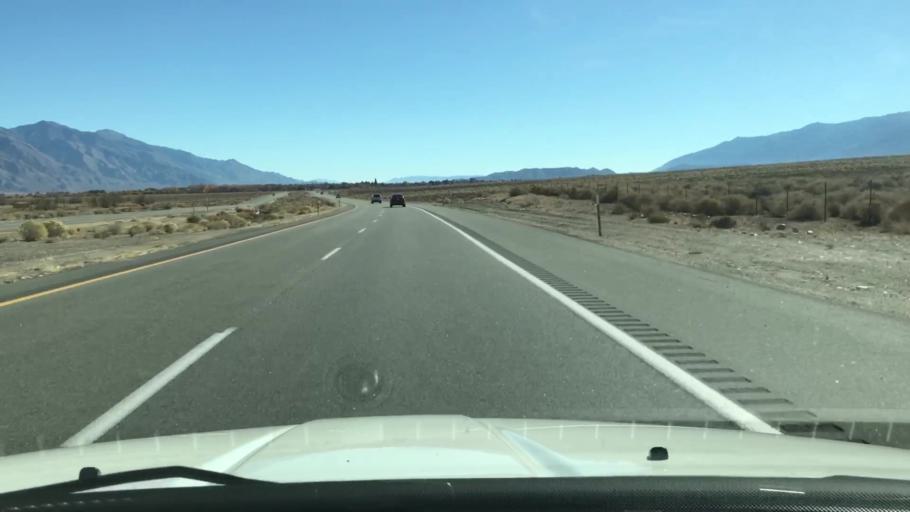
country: US
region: California
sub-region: Inyo County
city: Lone Pine
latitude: 36.8280
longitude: -118.2221
